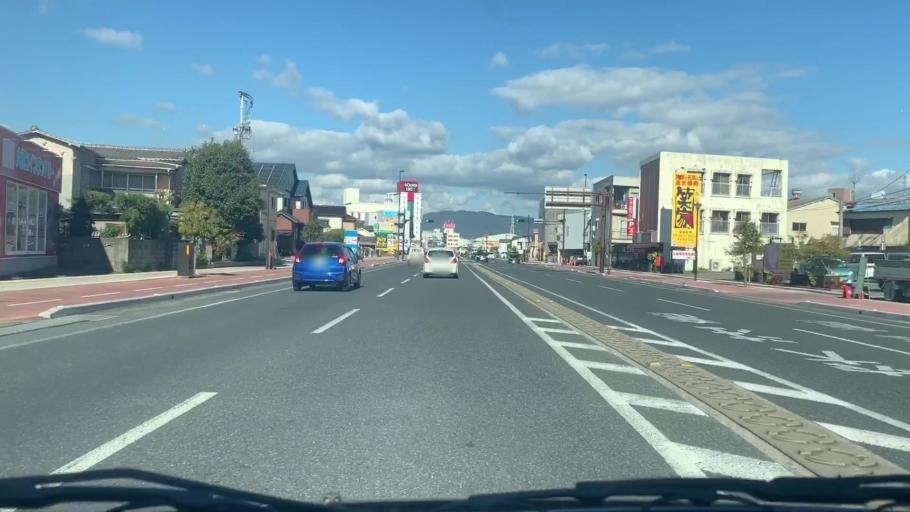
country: JP
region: Saga Prefecture
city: Saga-shi
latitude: 33.2677
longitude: 130.2937
